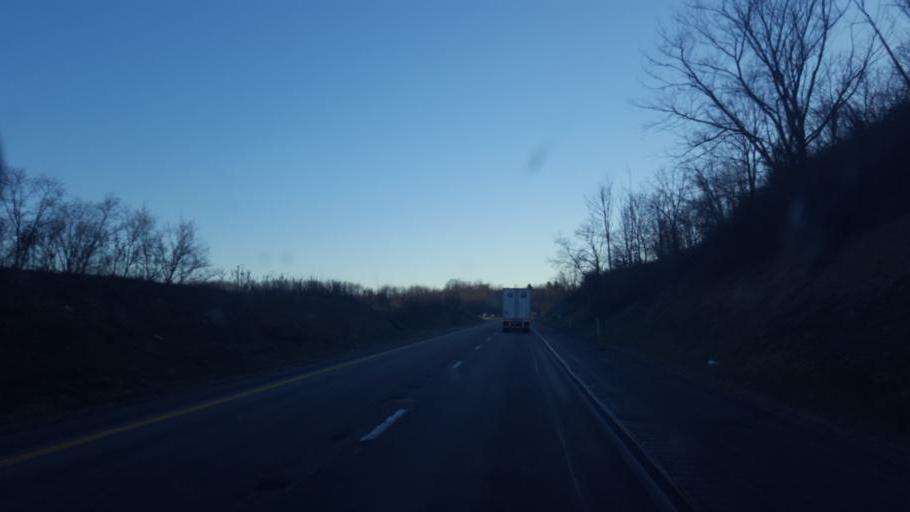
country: US
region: West Virginia
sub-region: Brooke County
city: Bethany
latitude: 40.1129
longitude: -80.4893
